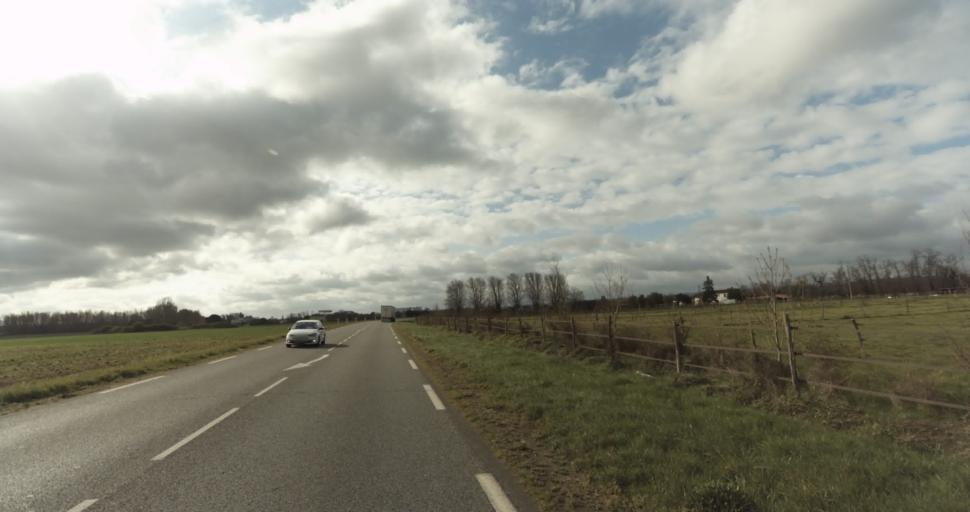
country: FR
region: Midi-Pyrenees
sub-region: Departement de la Haute-Garonne
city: Miremont
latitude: 43.3792
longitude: 1.4452
